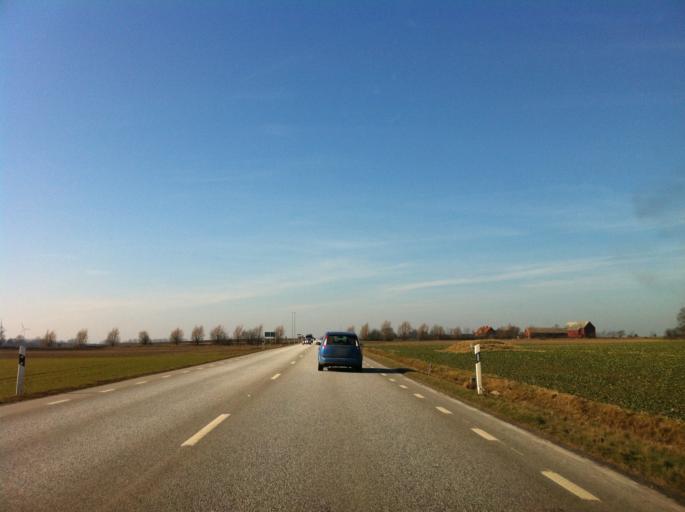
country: SE
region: Skane
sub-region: Landskrona
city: Asmundtorp
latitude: 55.8907
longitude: 12.9491
